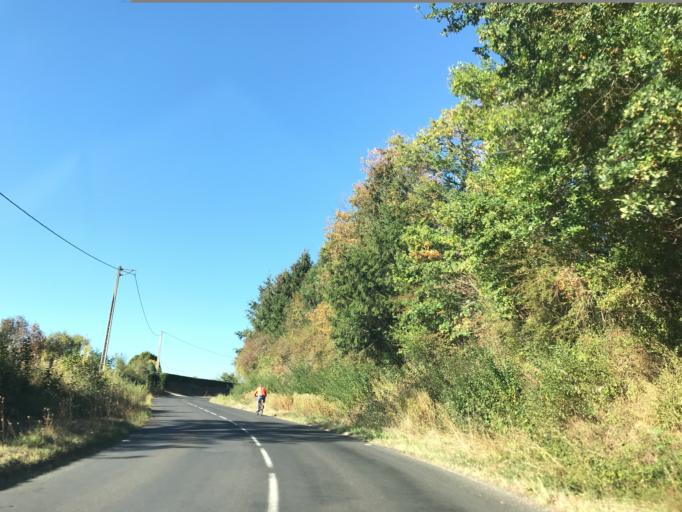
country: FR
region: Auvergne
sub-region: Departement du Puy-de-Dome
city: Escoutoux
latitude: 45.7796
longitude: 3.5985
